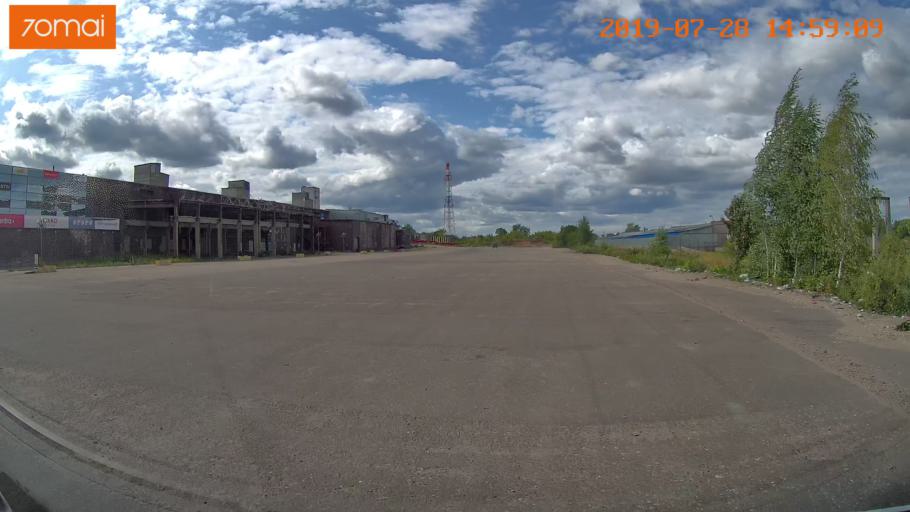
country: RU
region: Ivanovo
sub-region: Gorod Ivanovo
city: Ivanovo
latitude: 56.9675
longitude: 41.0267
